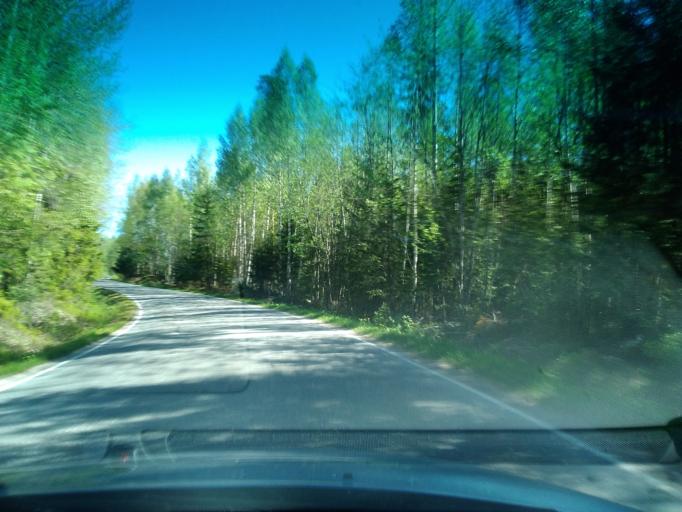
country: FI
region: Uusimaa
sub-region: Helsinki
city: Kaerkoelae
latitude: 60.6609
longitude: 23.9486
